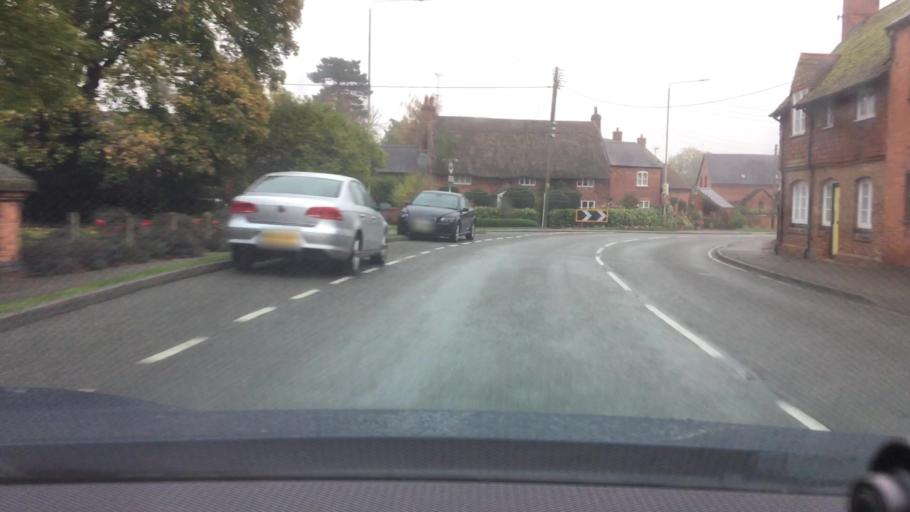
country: GB
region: England
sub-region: Leicestershire
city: Market Harborough
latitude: 52.4798
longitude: -0.9618
